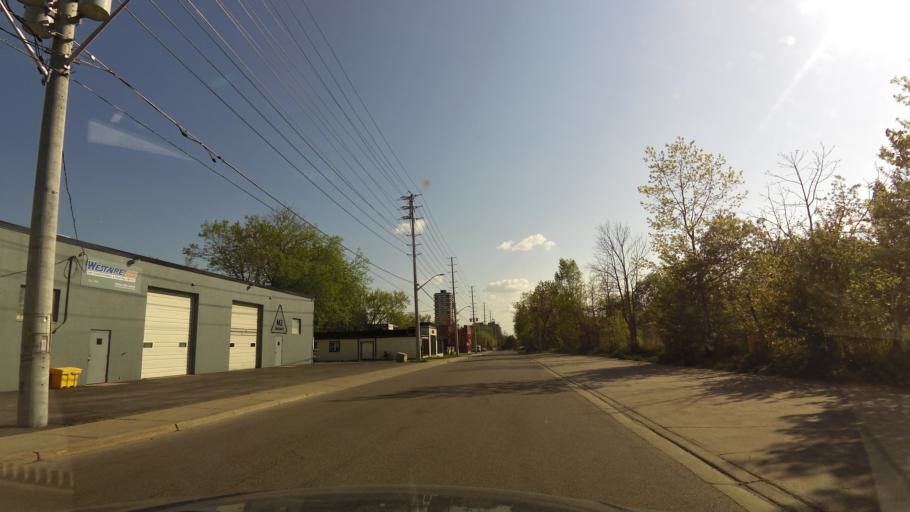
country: CA
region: Ontario
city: Mississauga
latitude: 43.5605
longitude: -79.5818
